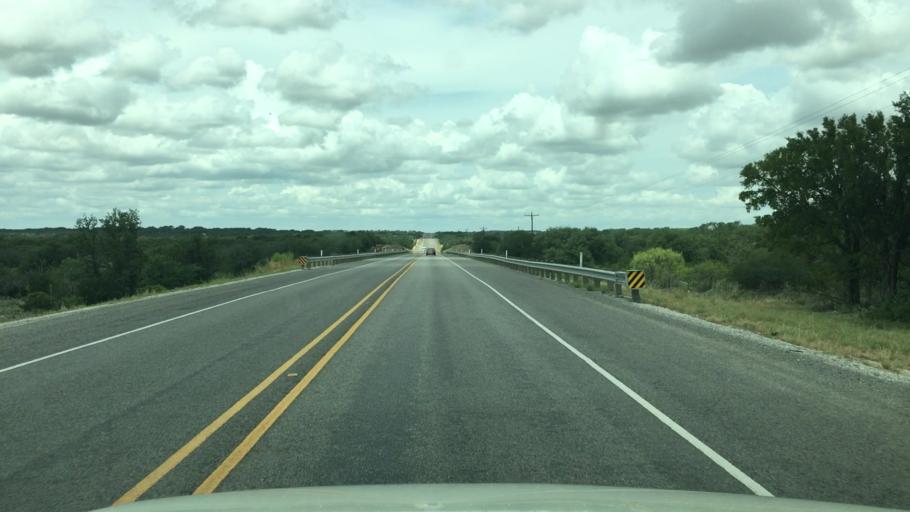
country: US
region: Texas
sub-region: McCulloch County
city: Brady
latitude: 31.0351
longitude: -99.2361
